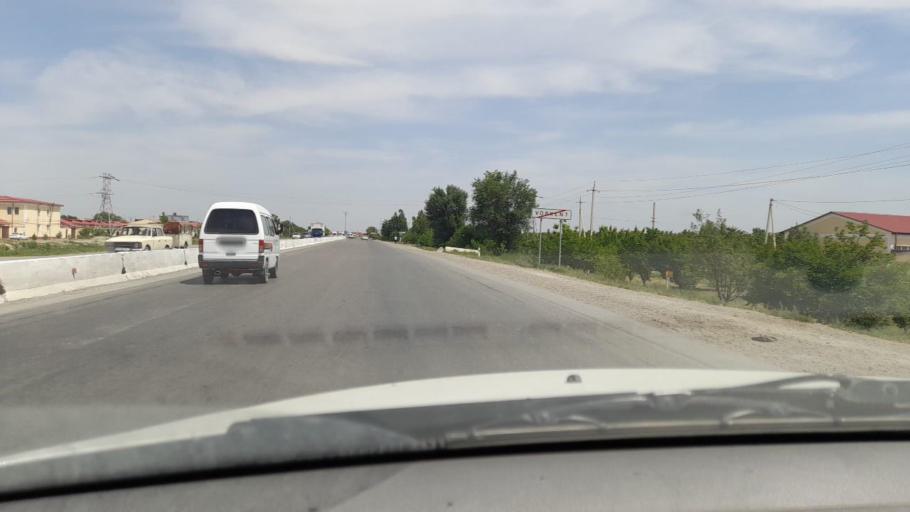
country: UZ
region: Bukhara
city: Wobkent
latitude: 40.0273
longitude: 64.5363
